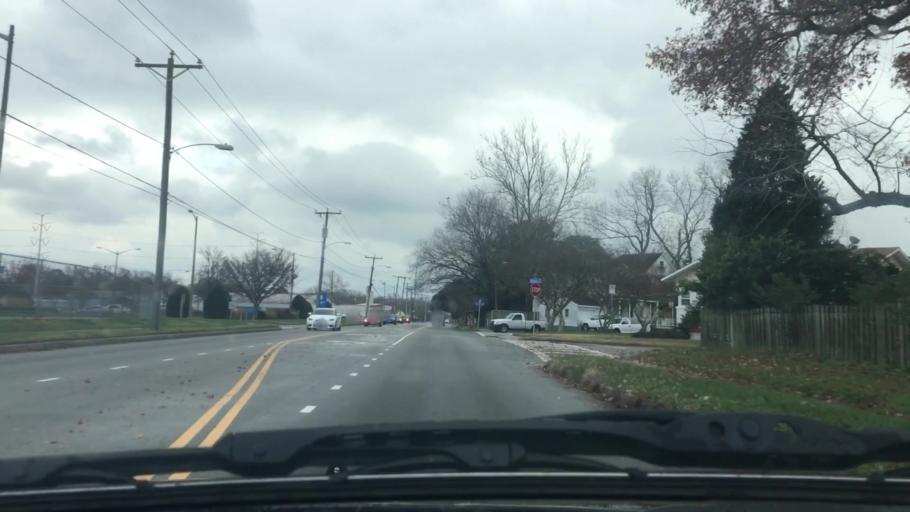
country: US
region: Virginia
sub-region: City of Norfolk
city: Norfolk
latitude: 36.8811
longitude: -76.2553
